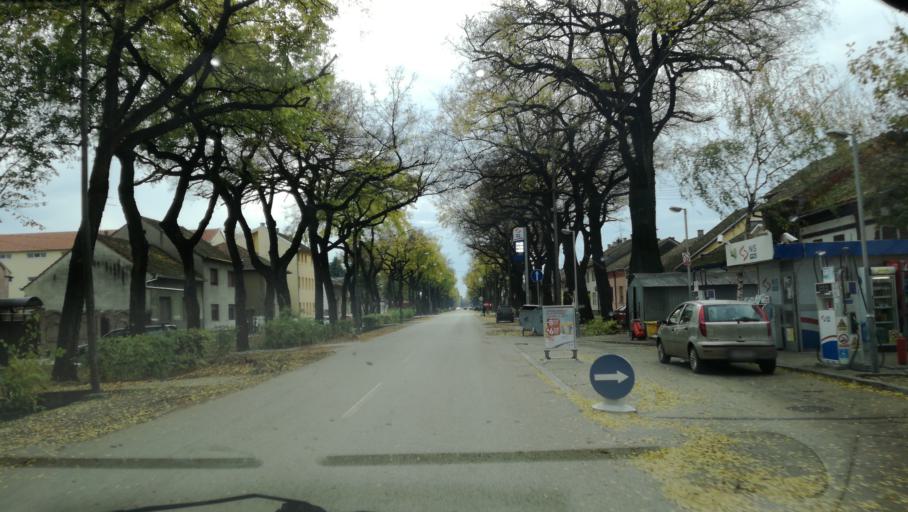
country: RS
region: Autonomna Pokrajina Vojvodina
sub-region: Severnobanatski Okrug
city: Kikinda
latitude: 45.8375
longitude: 20.4780
